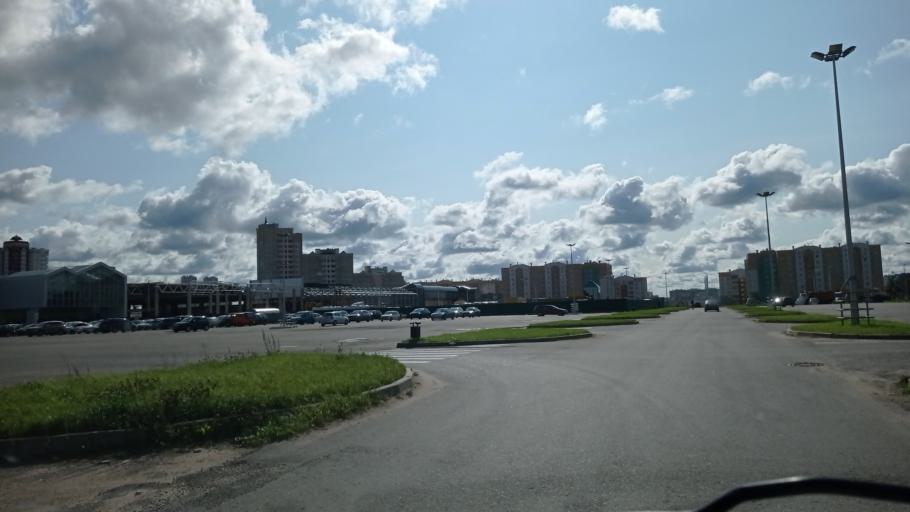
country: BY
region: Vitebsk
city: Vitebsk
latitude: 55.1758
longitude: 30.2640
